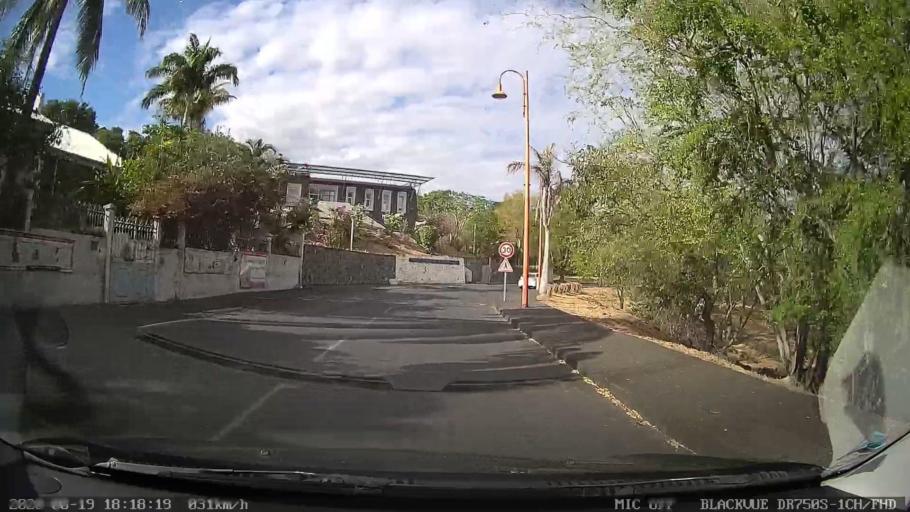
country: RE
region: Reunion
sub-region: Reunion
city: La Possession
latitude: -20.9476
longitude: 55.3328
